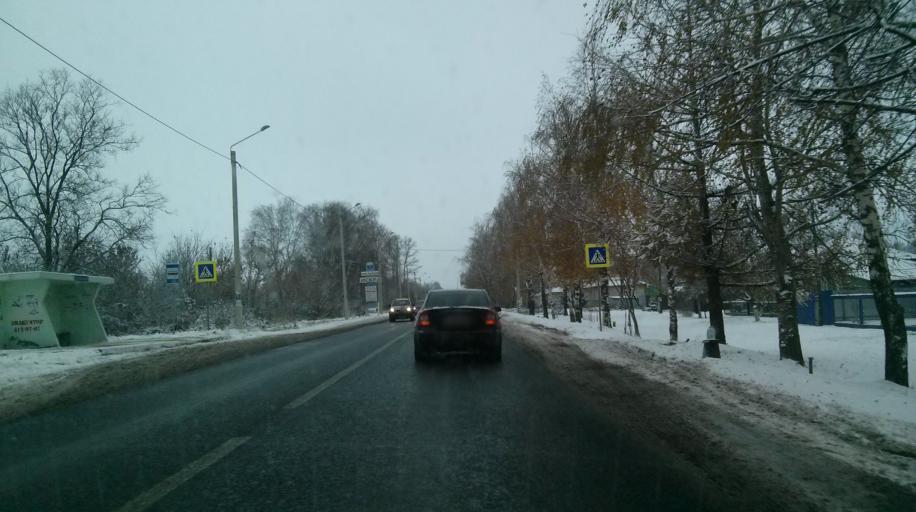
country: RU
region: Nizjnij Novgorod
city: Bogorodsk
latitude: 56.0631
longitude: 43.4227
